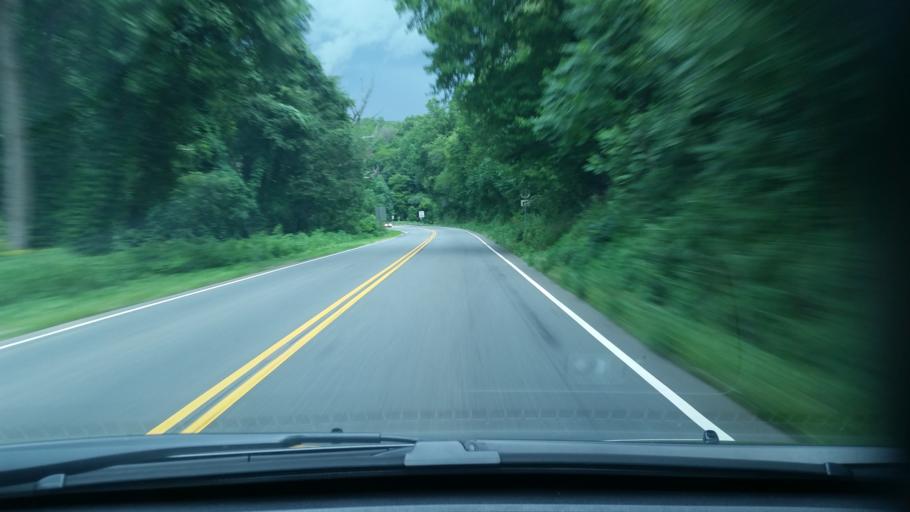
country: US
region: Virginia
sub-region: Nelson County
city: Nellysford
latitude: 37.8866
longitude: -78.8231
